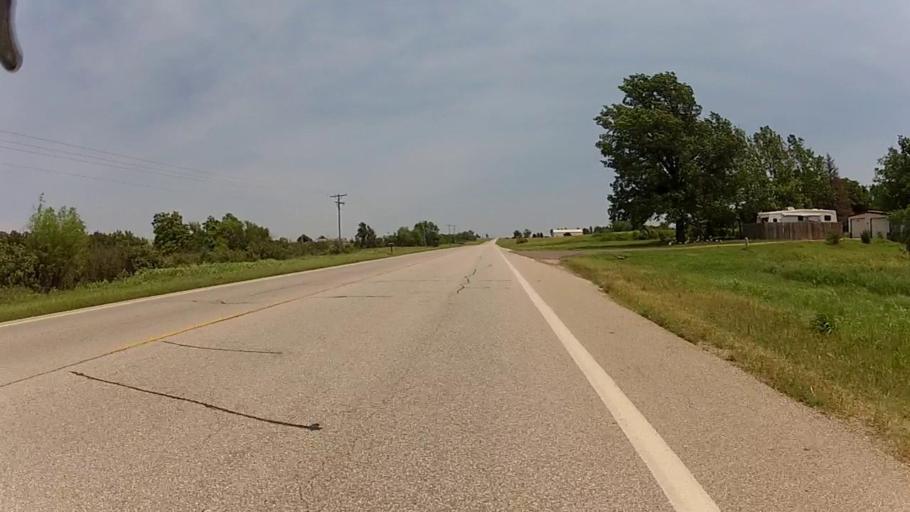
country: US
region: Kansas
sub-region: Cowley County
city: Arkansas City
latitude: 37.0563
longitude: -97.1155
